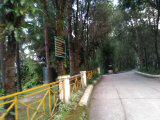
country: NP
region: Central Region
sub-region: Bagmati Zone
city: Kathmandu
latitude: 27.7743
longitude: 85.3586
